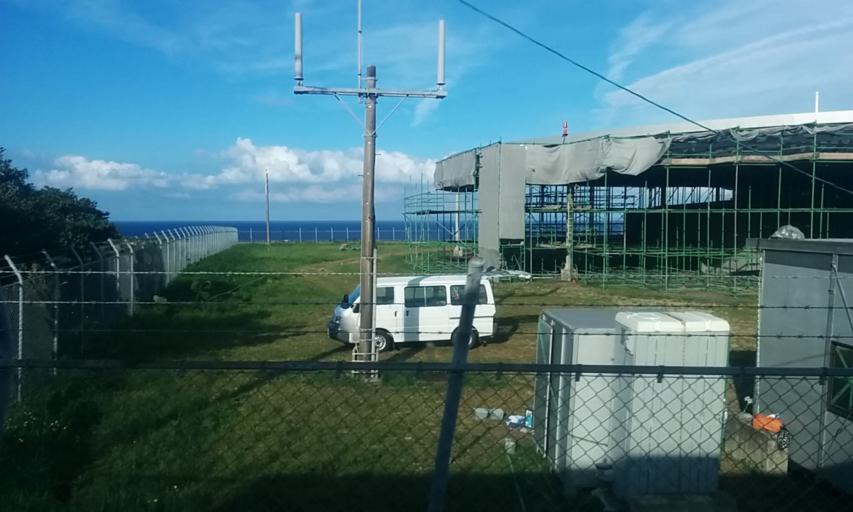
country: JP
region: Kagoshima
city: Nishinoomote
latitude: 30.3793
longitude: 130.6620
